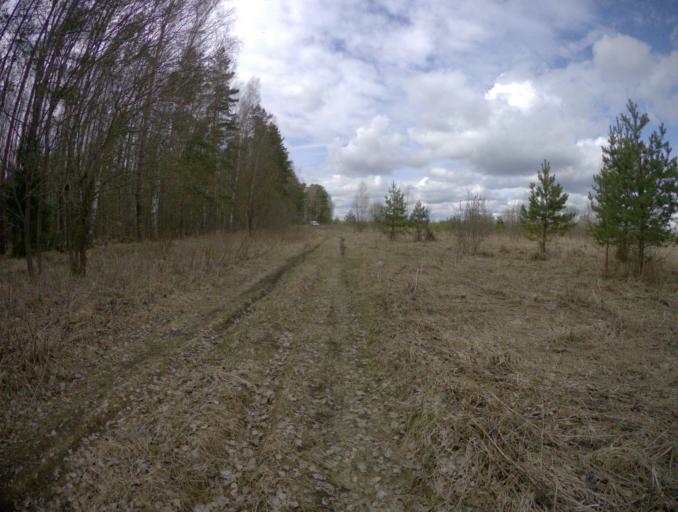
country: RU
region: Vladimir
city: Orgtrud
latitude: 56.0646
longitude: 40.6918
